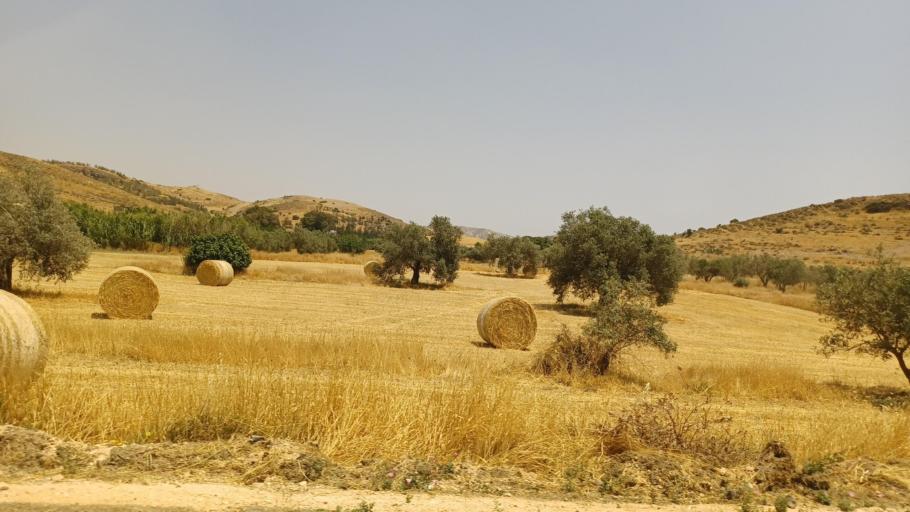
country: CY
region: Larnaka
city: Troulloi
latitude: 35.0235
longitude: 33.6119
